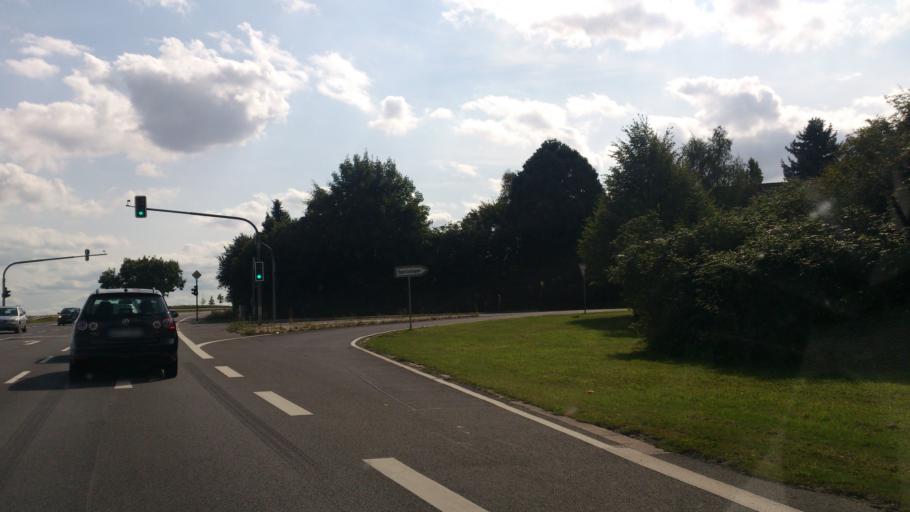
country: DE
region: North Rhine-Westphalia
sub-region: Regierungsbezirk Koln
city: Erftstadt
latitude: 50.7672
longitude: 6.7317
